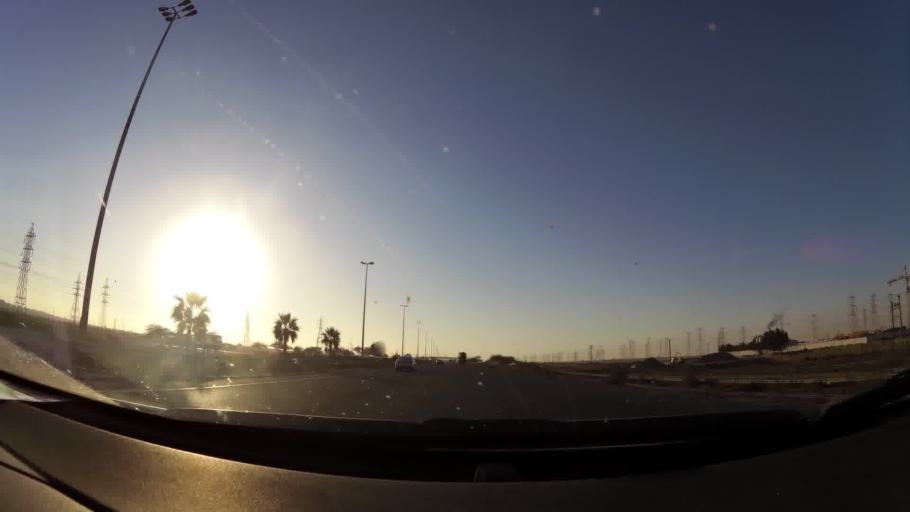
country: KW
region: Al Ahmadi
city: Al Fahahil
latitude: 28.8935
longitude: 48.2223
